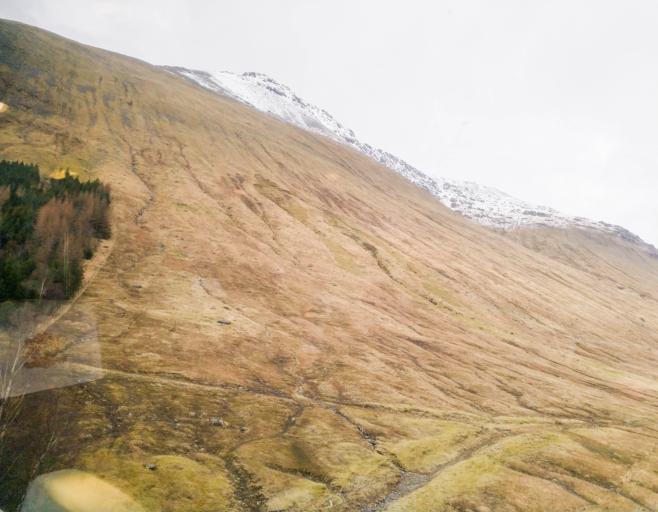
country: GB
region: Scotland
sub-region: Argyll and Bute
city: Garelochhead
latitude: 56.4893
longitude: -4.7061
